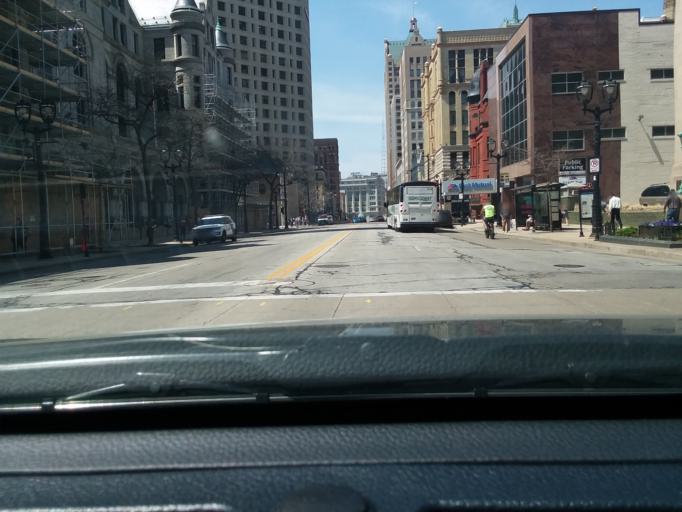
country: US
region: Wisconsin
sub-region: Milwaukee County
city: Milwaukee
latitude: 43.0389
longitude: -87.9041
